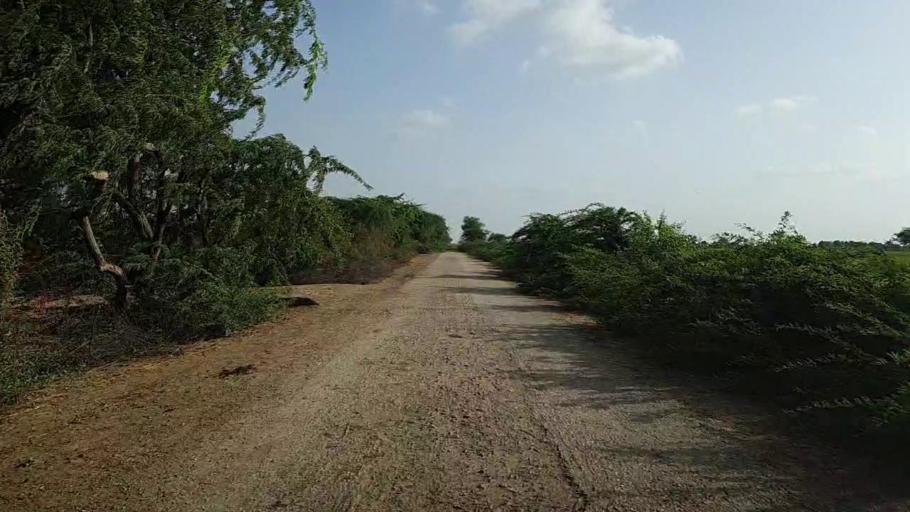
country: PK
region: Sindh
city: Kario
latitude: 24.6504
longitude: 68.4982
